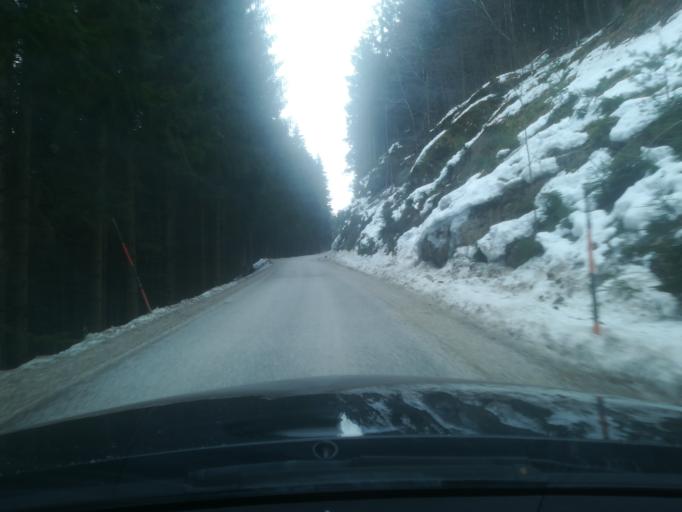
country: AT
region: Upper Austria
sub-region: Politischer Bezirk Perg
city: Perg
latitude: 48.4173
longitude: 14.6536
